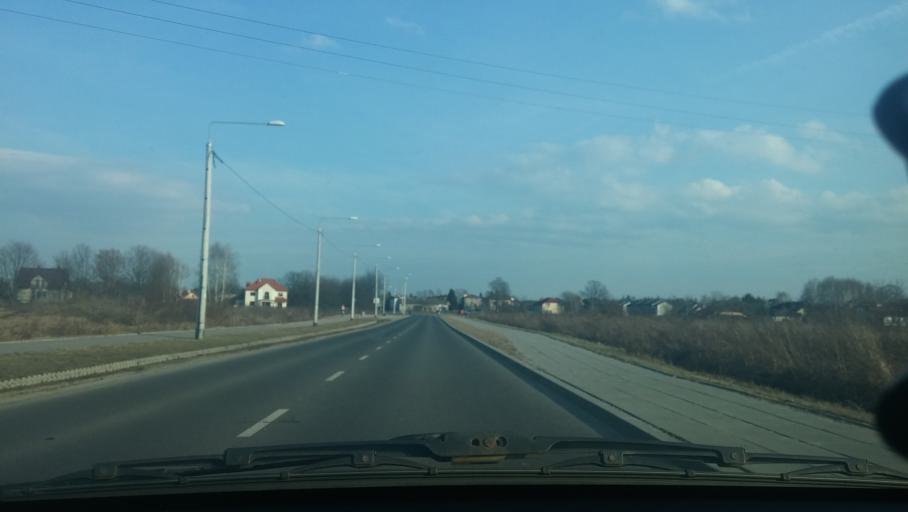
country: PL
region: Masovian Voivodeship
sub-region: Warszawa
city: Wawer
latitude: 52.1847
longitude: 21.1657
